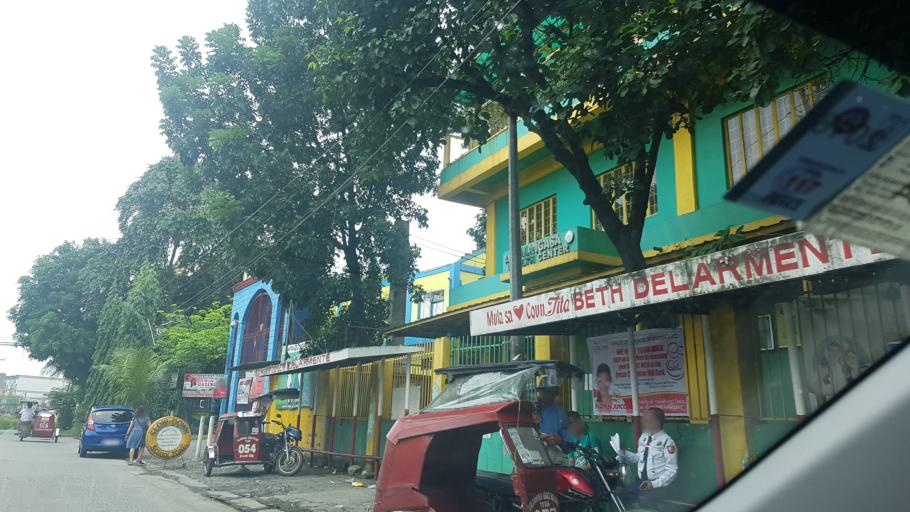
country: PH
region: Calabarzon
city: Del Monte
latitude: 14.6484
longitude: 121.0045
